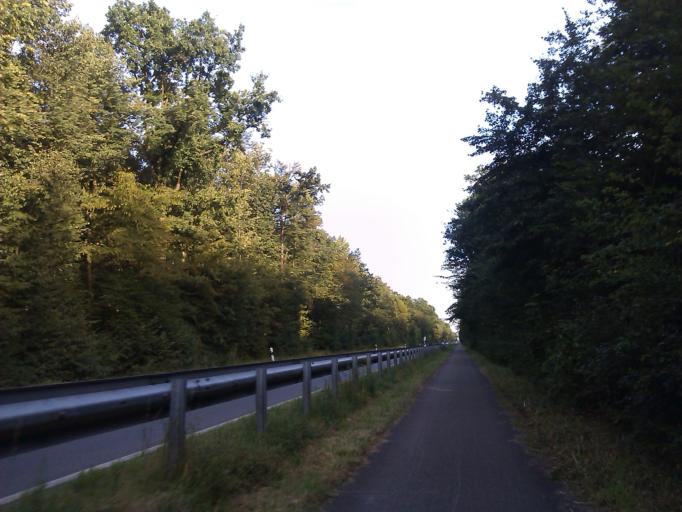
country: DE
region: Baden-Wuerttemberg
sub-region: Karlsruhe Region
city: Oftersheim
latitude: 49.3525
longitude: 8.5933
